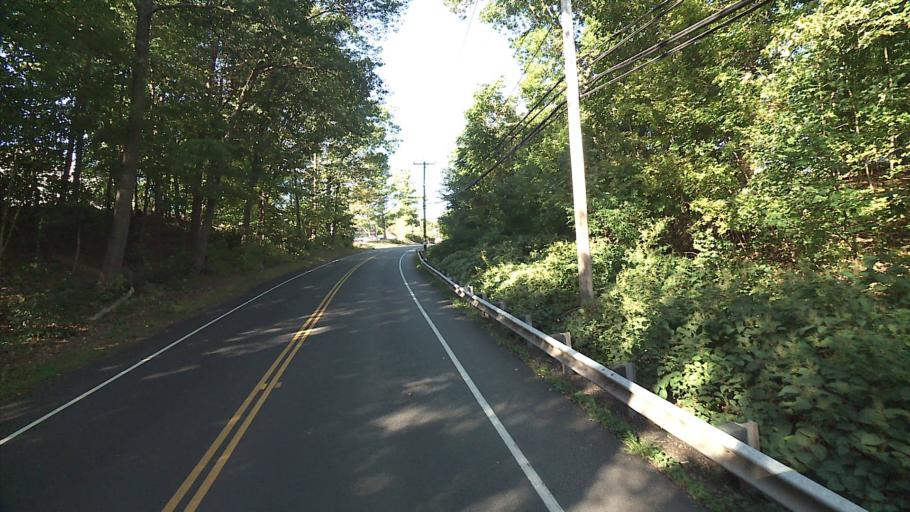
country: US
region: Connecticut
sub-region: New Haven County
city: Cheshire
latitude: 41.4986
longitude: -72.8980
